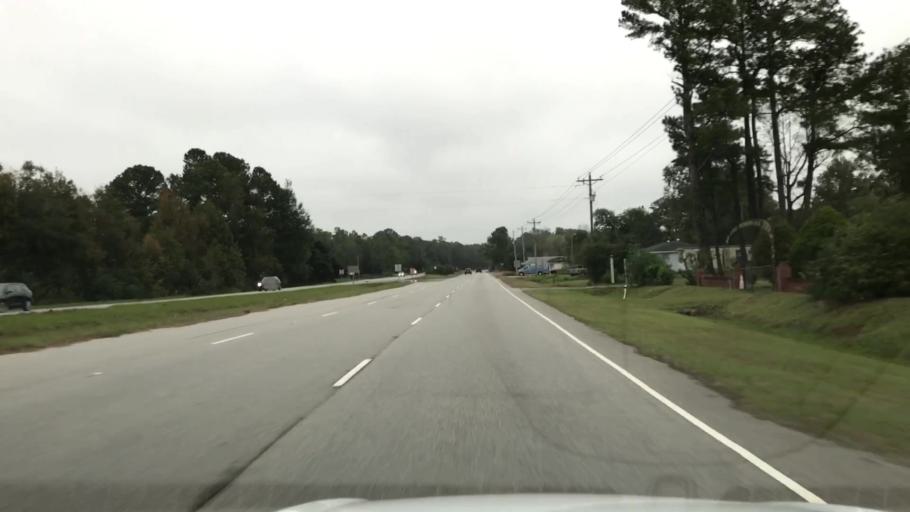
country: US
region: South Carolina
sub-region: Charleston County
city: Awendaw
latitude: 33.0282
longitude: -79.6272
